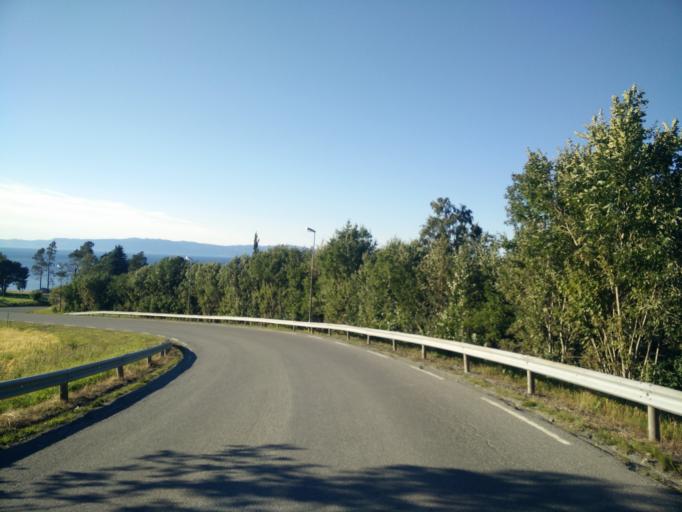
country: NO
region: Sor-Trondelag
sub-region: Malvik
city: Malvik
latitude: 63.4314
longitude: 10.5816
